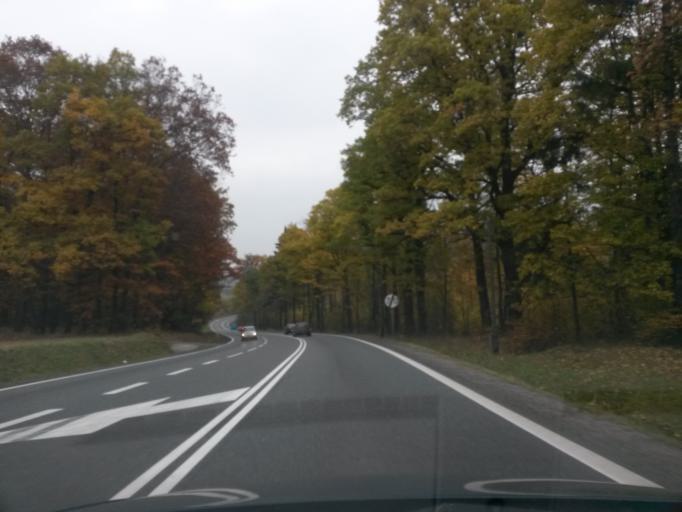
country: PL
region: Lower Silesian Voivodeship
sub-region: Powiat zabkowicki
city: Bardo
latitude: 50.4908
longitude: 16.7198
